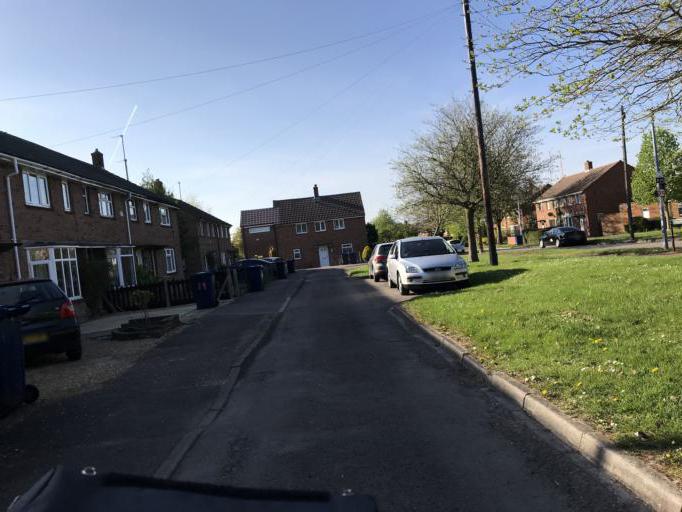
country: GB
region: England
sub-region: Cambridgeshire
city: Cambridge
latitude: 52.1814
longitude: 0.1603
